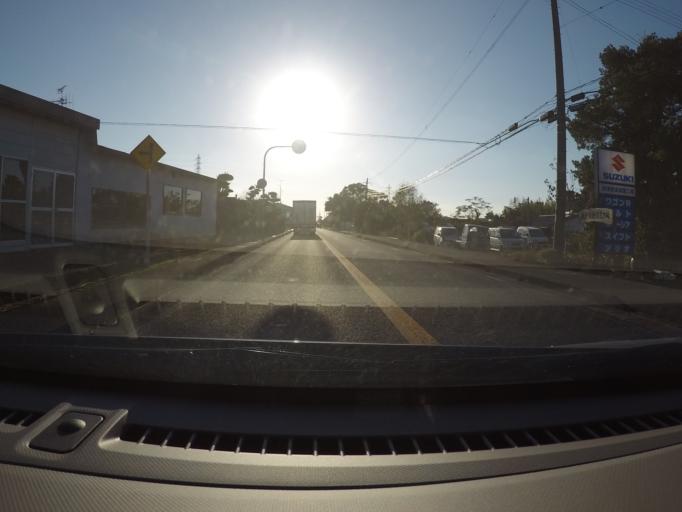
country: JP
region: Kagoshima
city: Izumi
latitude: 32.0960
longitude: 130.3001
